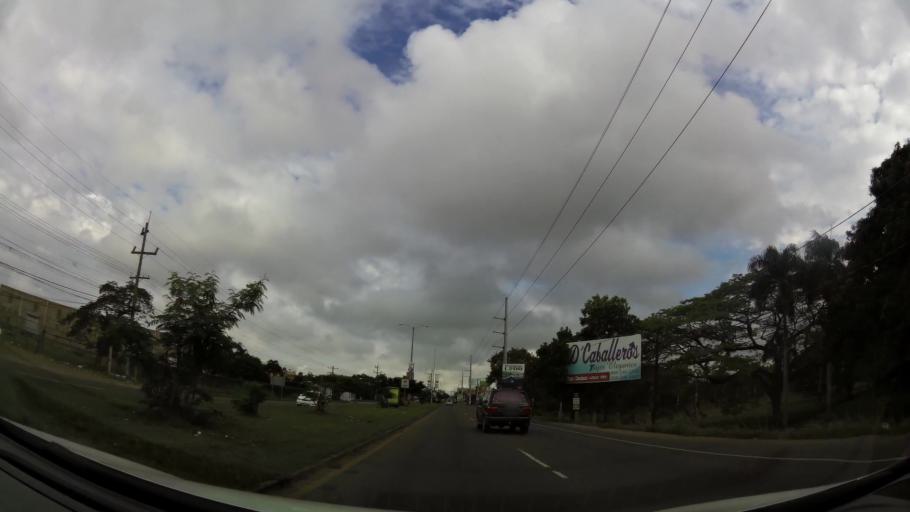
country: DO
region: Santiago
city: Licey al Medio
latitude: 19.4191
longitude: -70.6470
